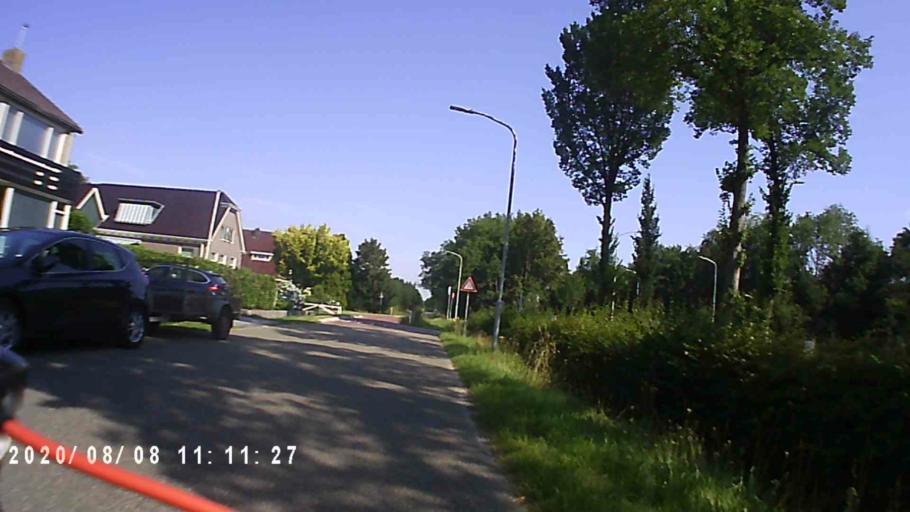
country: NL
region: Groningen
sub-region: Gemeente Leek
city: Leek
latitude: 53.1710
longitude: 6.3809
